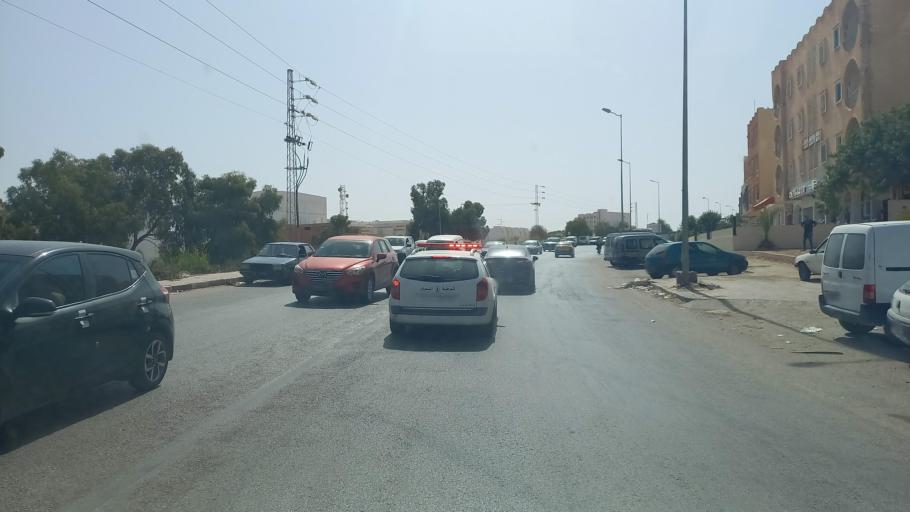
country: TN
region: Madanin
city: Medenine
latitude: 33.3442
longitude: 10.5018
